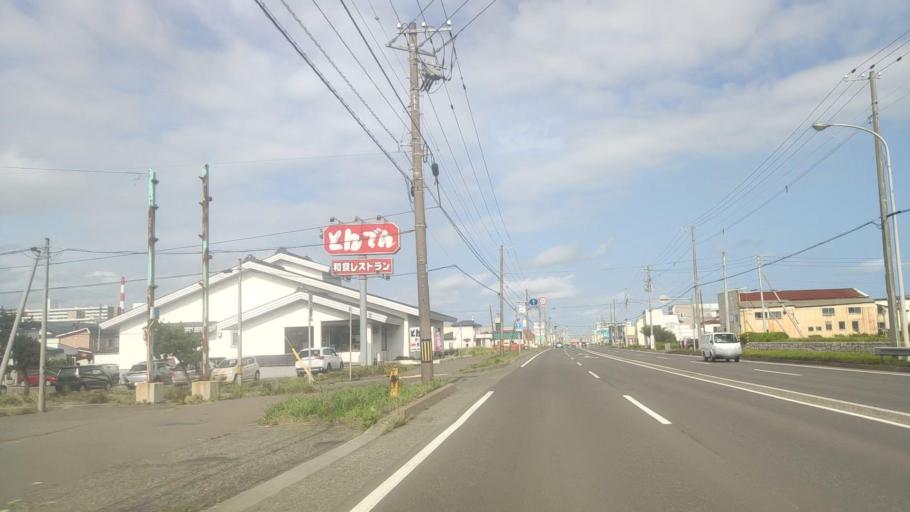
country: JP
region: Hokkaido
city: Tomakomai
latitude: 42.6233
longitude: 141.5724
